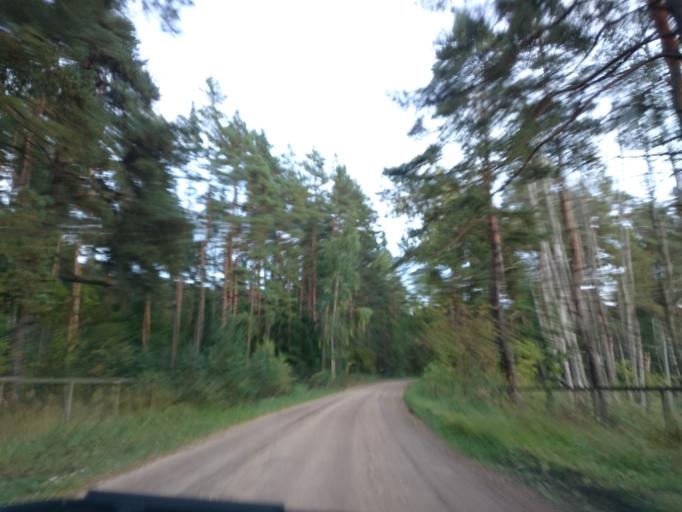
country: LV
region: Garkalne
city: Garkalne
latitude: 57.0497
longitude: 24.3799
